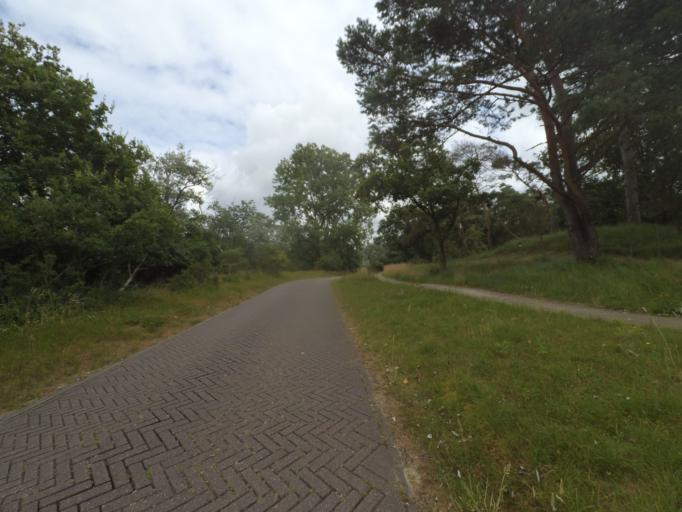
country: NL
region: South Holland
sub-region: Gemeente Leidschendam-Voorburg
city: Voorburg
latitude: 52.1256
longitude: 4.3322
